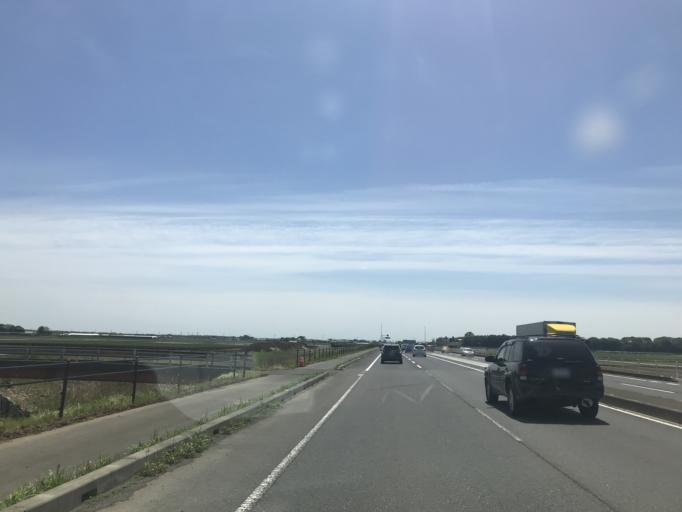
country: JP
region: Ibaraki
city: Shimodate
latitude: 36.2370
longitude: 139.9846
